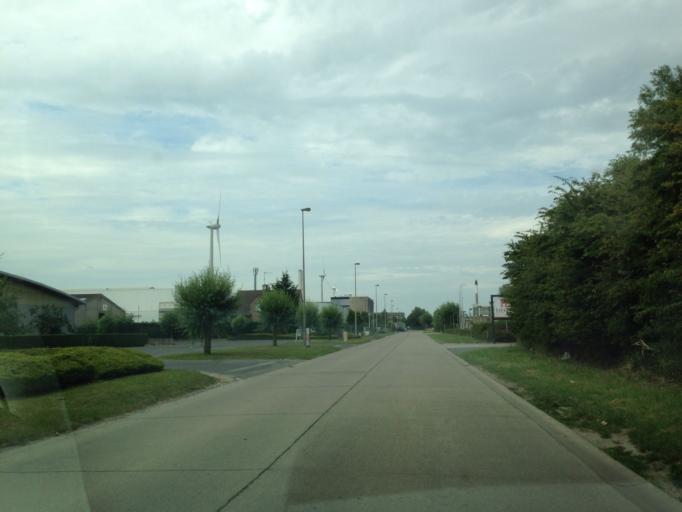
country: BE
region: Flanders
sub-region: Provincie West-Vlaanderen
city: Brugge
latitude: 51.2467
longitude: 3.2098
